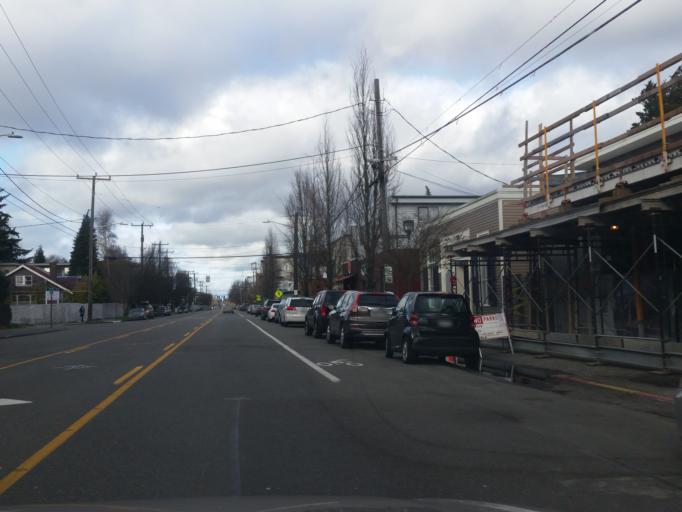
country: US
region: Washington
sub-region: King County
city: Seattle
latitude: 47.6789
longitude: -122.3553
